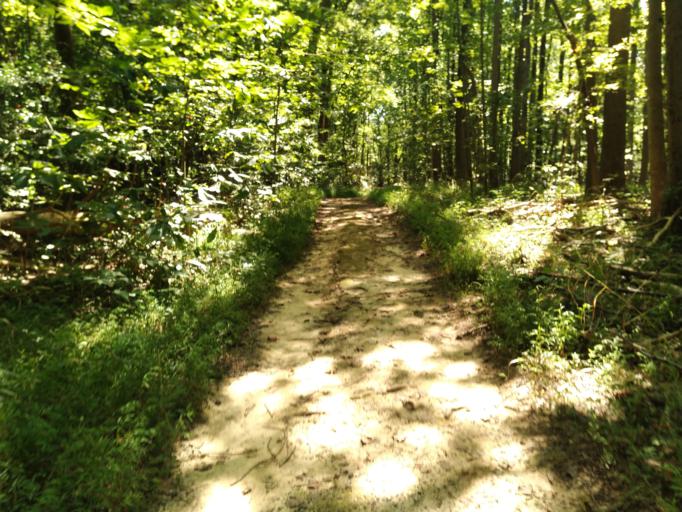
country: US
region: Maryland
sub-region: Calvert County
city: Prince Frederick
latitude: 38.5387
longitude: -76.5380
